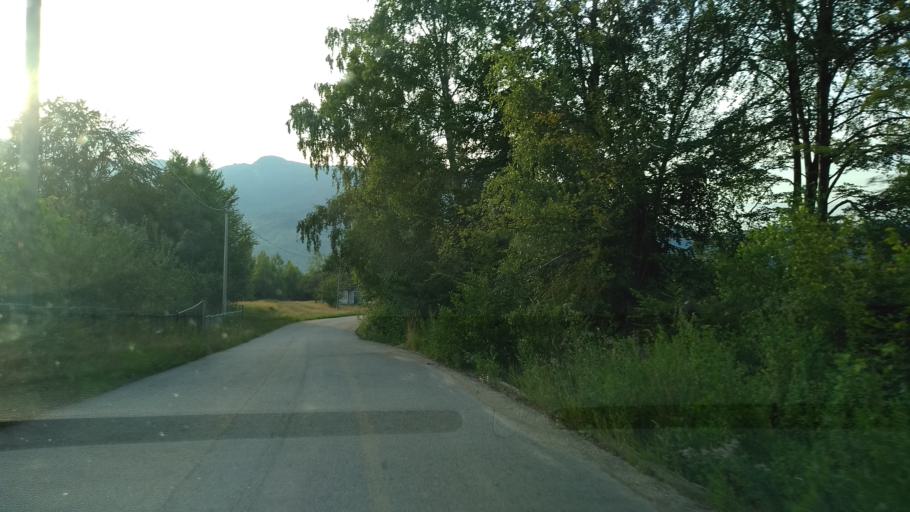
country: RO
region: Hunedoara
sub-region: Municipiul  Vulcan
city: Jiu-Paroseni
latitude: 45.3603
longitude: 23.2865
